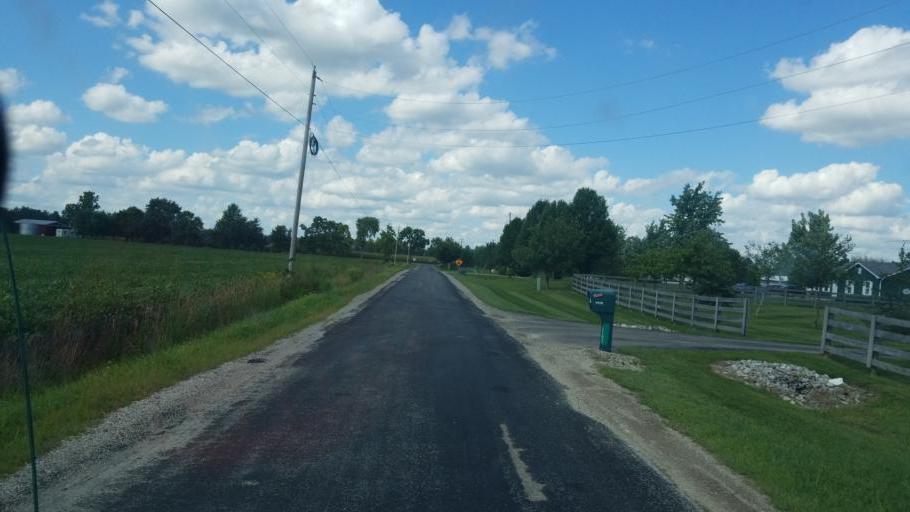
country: US
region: Ohio
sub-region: Union County
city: Richwood
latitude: 40.3134
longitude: -83.2218
